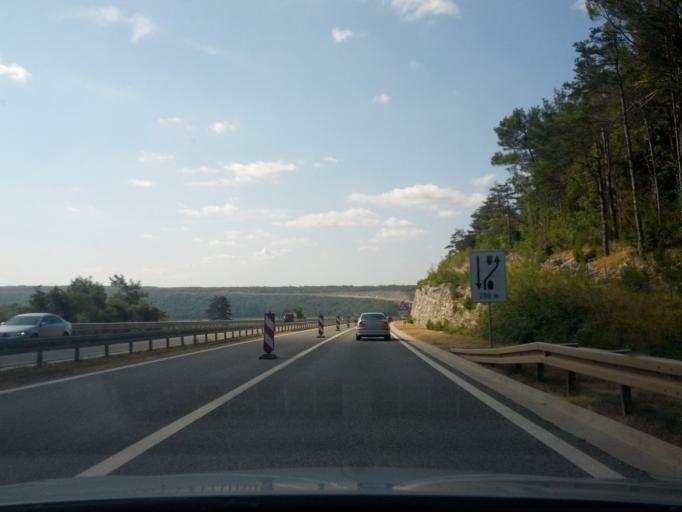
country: HR
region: Istarska
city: Novigrad
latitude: 45.3452
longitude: 13.6227
